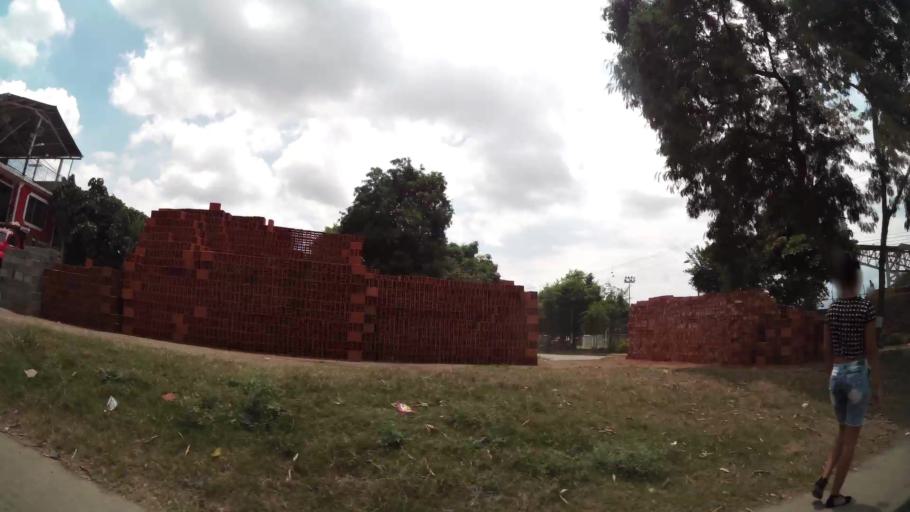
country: CO
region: Valle del Cauca
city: Cali
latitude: 3.4521
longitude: -76.4779
